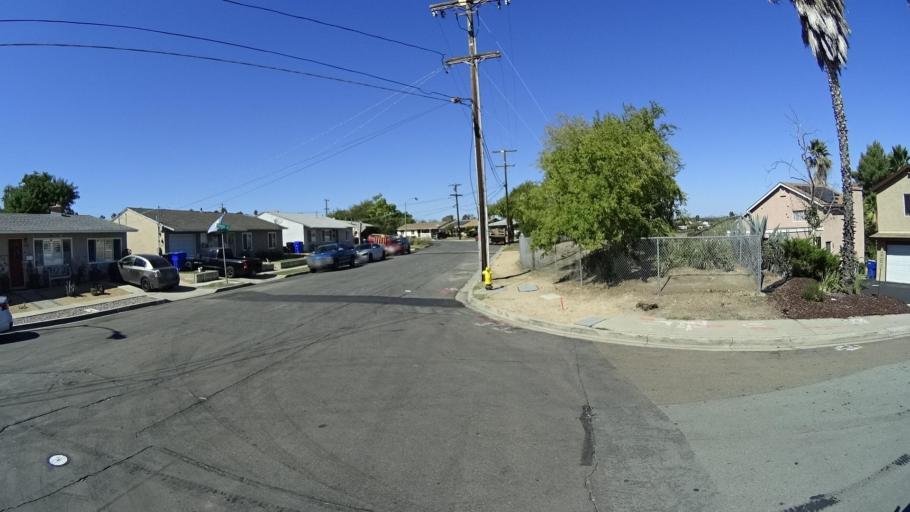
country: US
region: California
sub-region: San Diego County
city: La Presa
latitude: 32.7147
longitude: -117.0231
